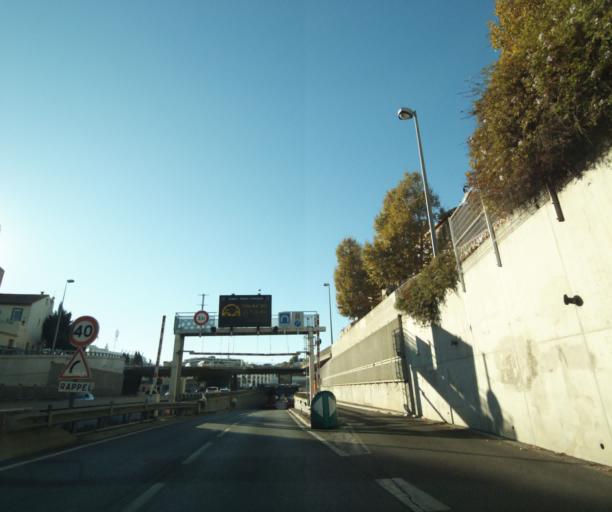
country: FR
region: Provence-Alpes-Cote d'Azur
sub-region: Departement des Bouches-du-Rhone
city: Marseille 05
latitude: 43.2828
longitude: 5.3957
